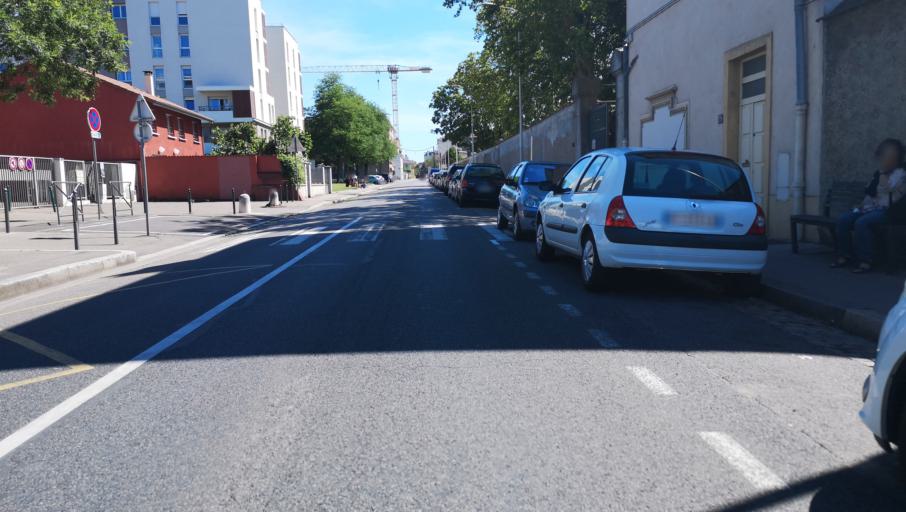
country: FR
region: Rhone-Alpes
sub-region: Departement du Rhone
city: Caluire-et-Cuire
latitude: 45.7833
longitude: 4.8208
